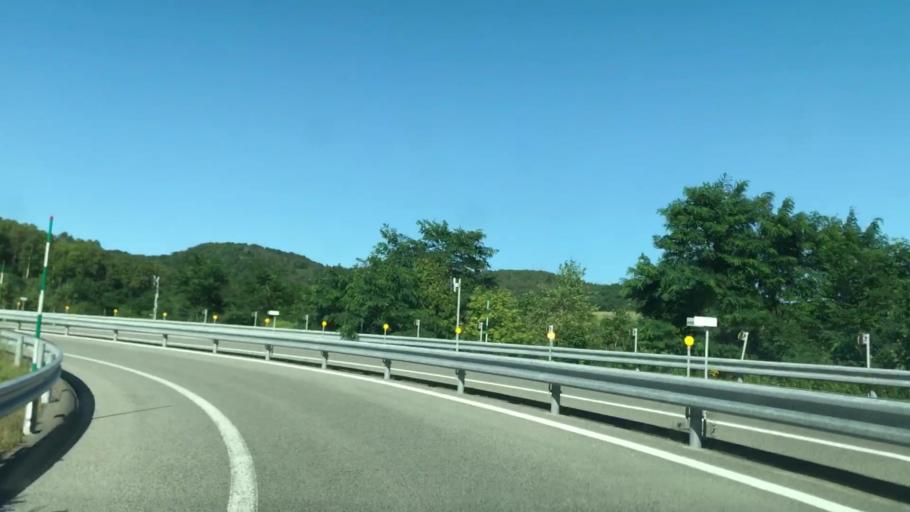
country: JP
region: Hokkaido
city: Date
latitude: 42.5570
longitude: 140.7724
